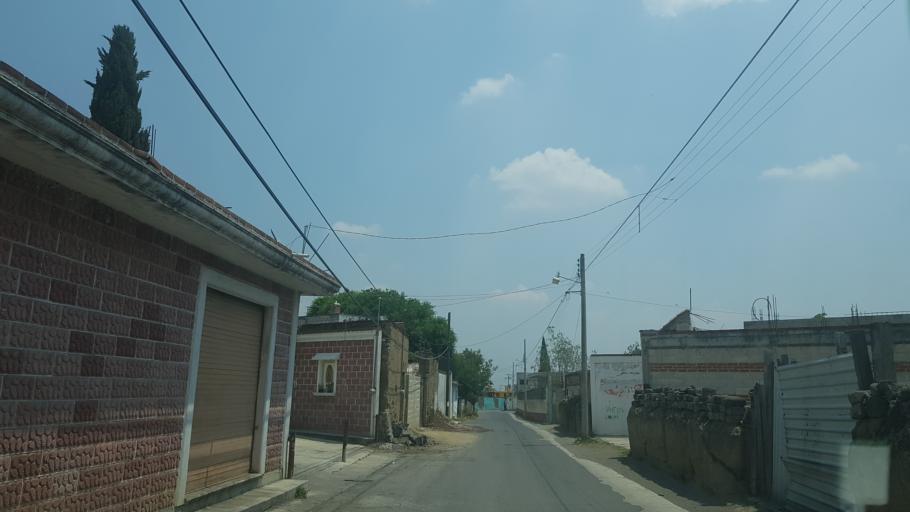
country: MX
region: Puebla
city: San Andres Calpan
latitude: 19.1052
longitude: -98.4672
